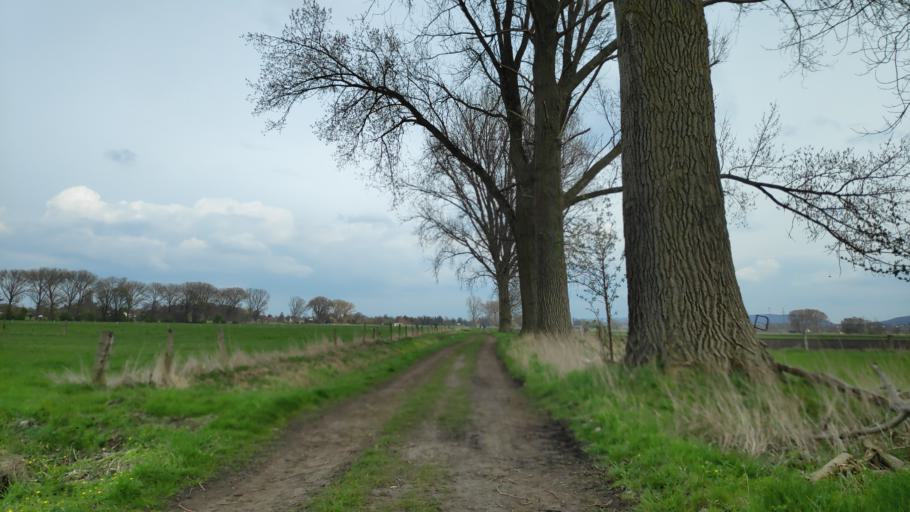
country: DE
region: North Rhine-Westphalia
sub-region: Regierungsbezirk Detmold
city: Minden
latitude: 52.2918
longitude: 8.8497
